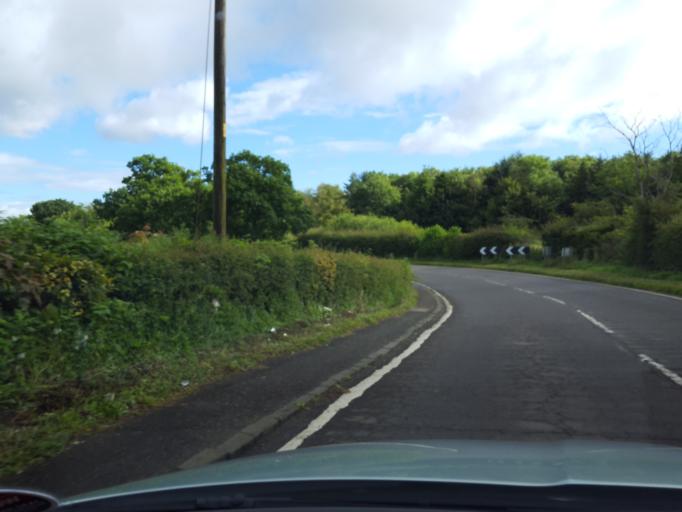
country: GB
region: Scotland
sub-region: West Lothian
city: Linlithgow
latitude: 55.9965
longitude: -3.6084
